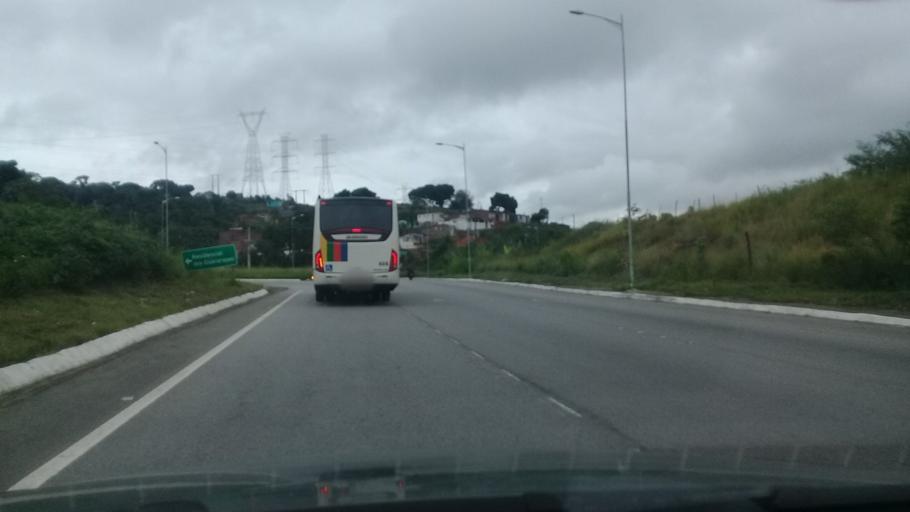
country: BR
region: Pernambuco
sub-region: Jaboatao Dos Guararapes
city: Jaboatao dos Guararapes
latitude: -8.0815
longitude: -34.9914
